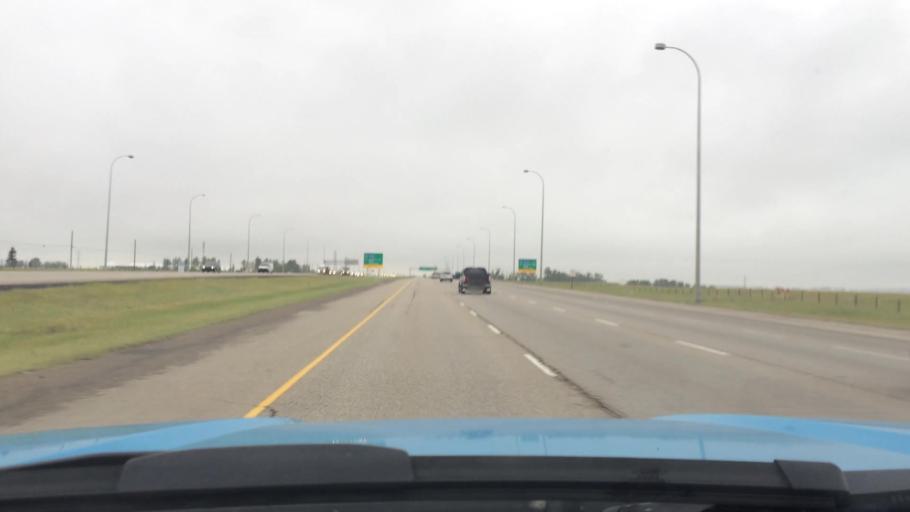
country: CA
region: Alberta
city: Airdrie
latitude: 51.1928
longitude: -114.0017
